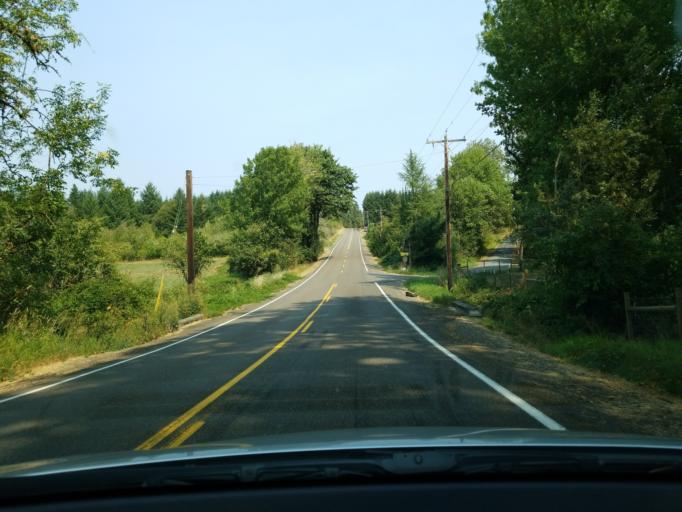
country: US
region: Oregon
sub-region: Marion County
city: Aumsville
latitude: 44.9287
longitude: -122.8755
